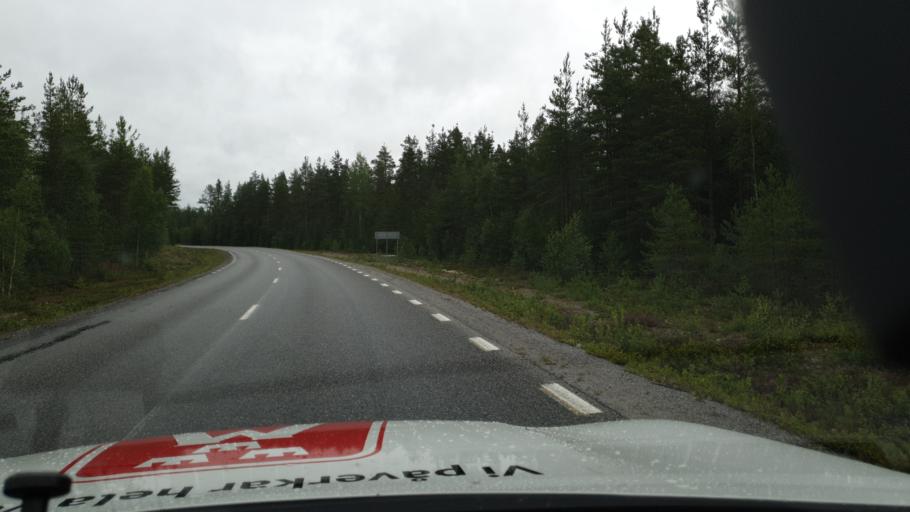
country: SE
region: Vaesterbotten
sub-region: Umea Kommun
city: Saevar
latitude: 63.9191
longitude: 20.5404
